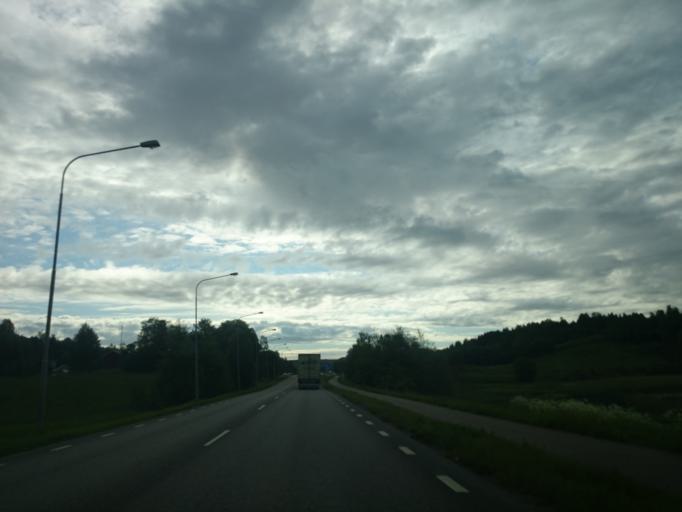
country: SE
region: Vaesternorrland
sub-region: Sundsvalls Kommun
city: Johannedal
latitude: 62.4132
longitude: 17.3625
